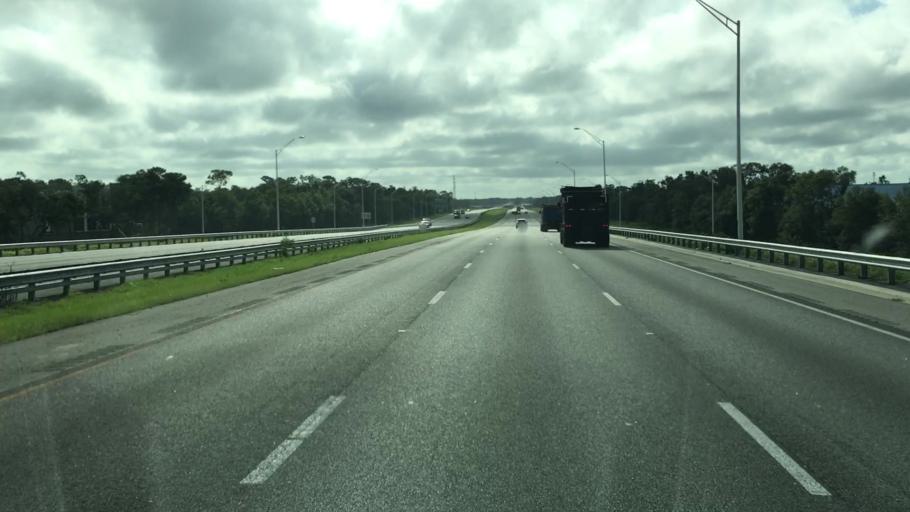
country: US
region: Florida
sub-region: Volusia County
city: Port Orange
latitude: 29.1042
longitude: -81.0279
